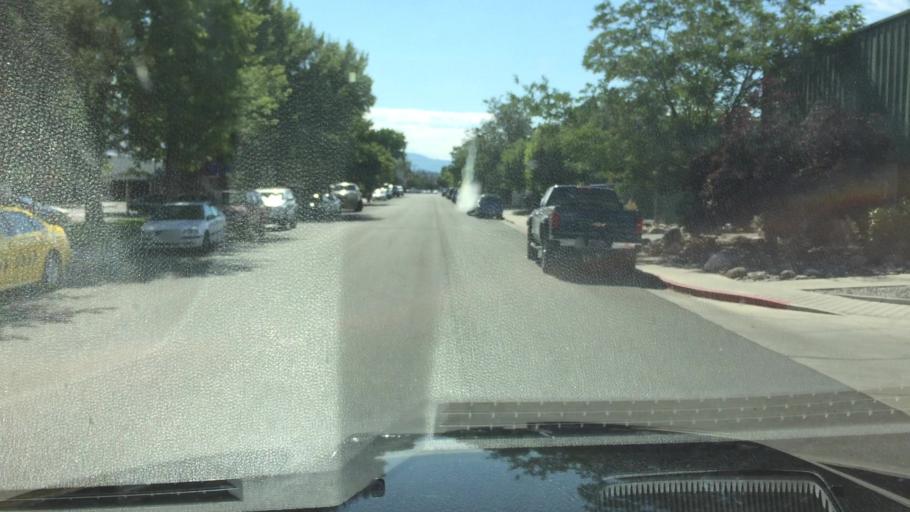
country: US
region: Nevada
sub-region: Washoe County
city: Reno
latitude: 39.4997
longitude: -119.7862
